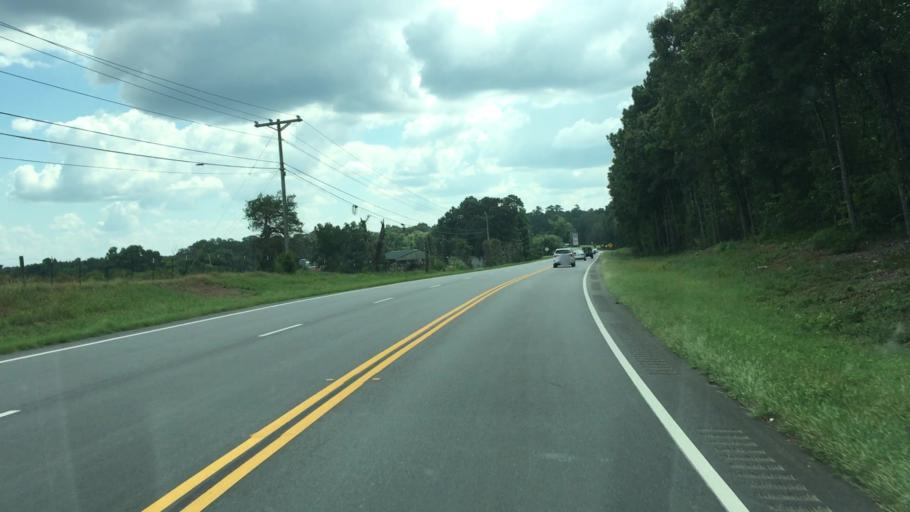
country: US
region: Georgia
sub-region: Putnam County
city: Jefferson
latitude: 33.4230
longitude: -83.3704
